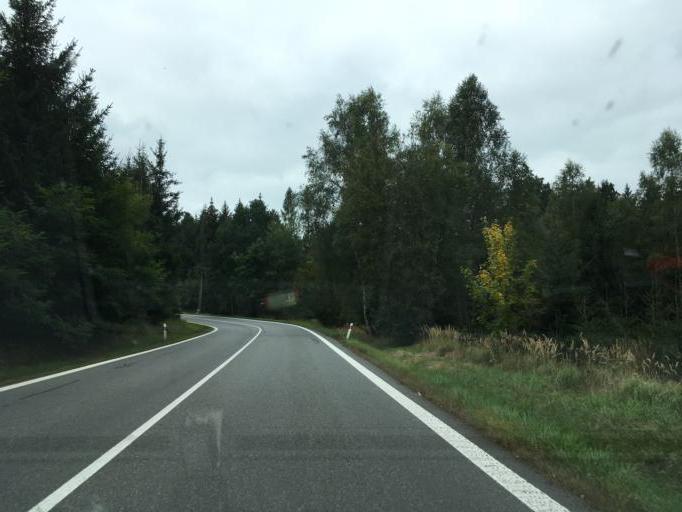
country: CZ
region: Central Bohemia
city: Cechtice
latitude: 49.5742
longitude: 15.1004
